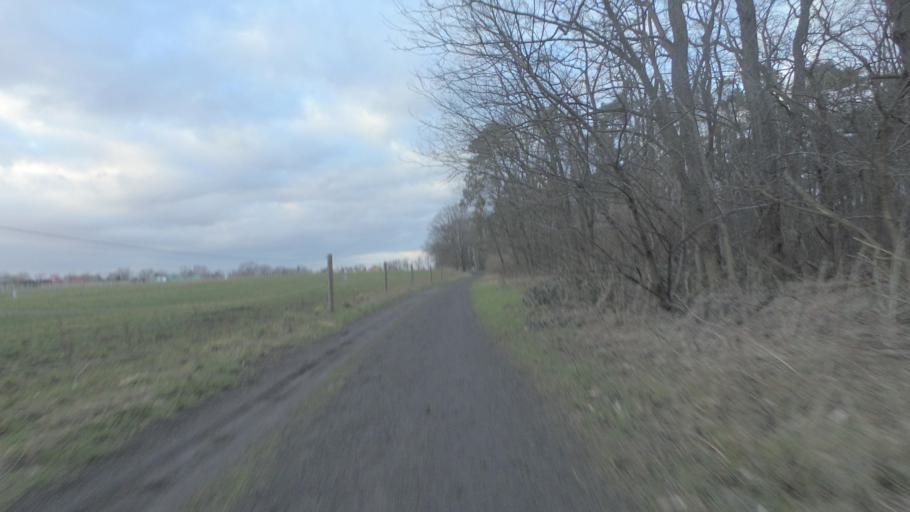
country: DE
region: Brandenburg
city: Rangsdorf
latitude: 52.2668
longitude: 13.3570
